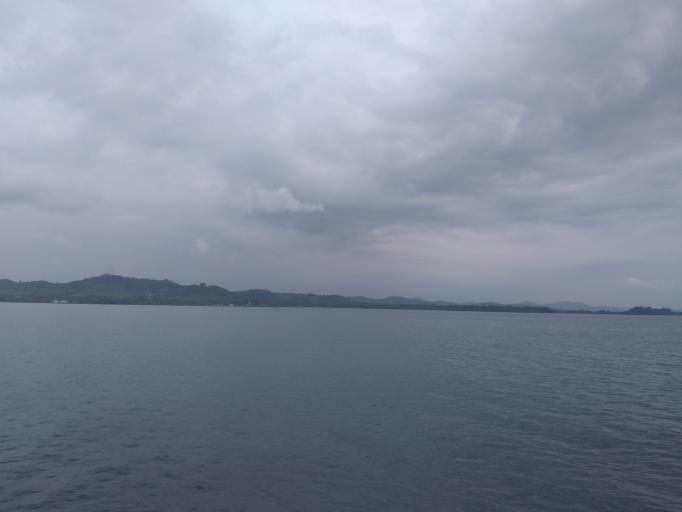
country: TH
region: Trat
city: Laem Ngop
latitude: 12.1657
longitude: 102.2943
